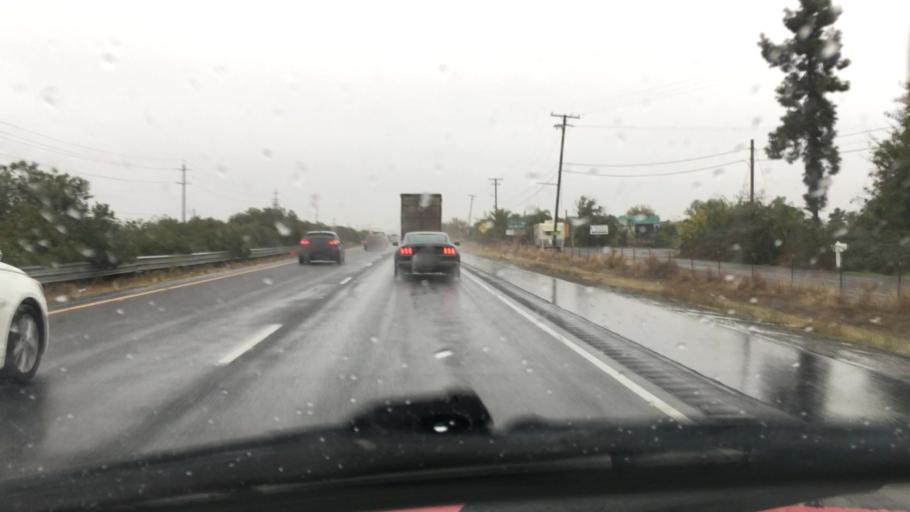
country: US
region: California
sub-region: Sacramento County
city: Galt
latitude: 38.3066
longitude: -121.3195
